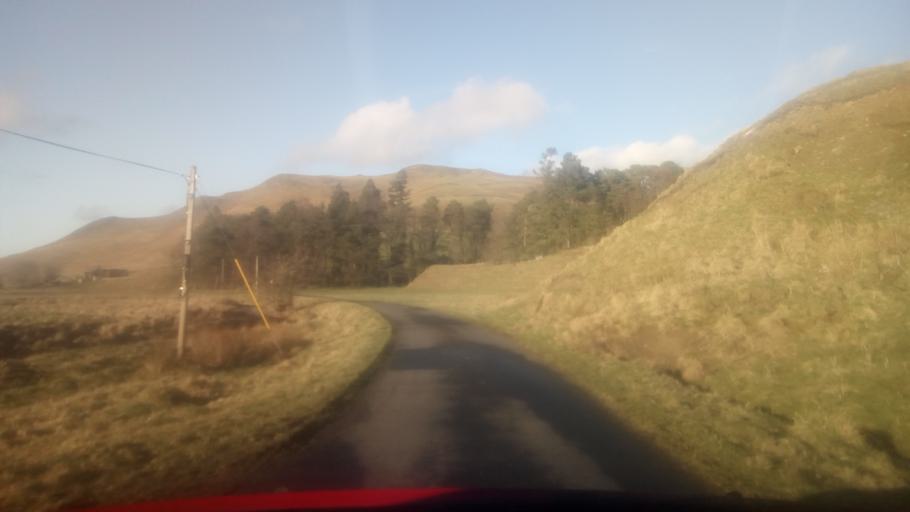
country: GB
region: England
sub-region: Northumberland
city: Rochester
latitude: 55.3854
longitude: -2.3738
